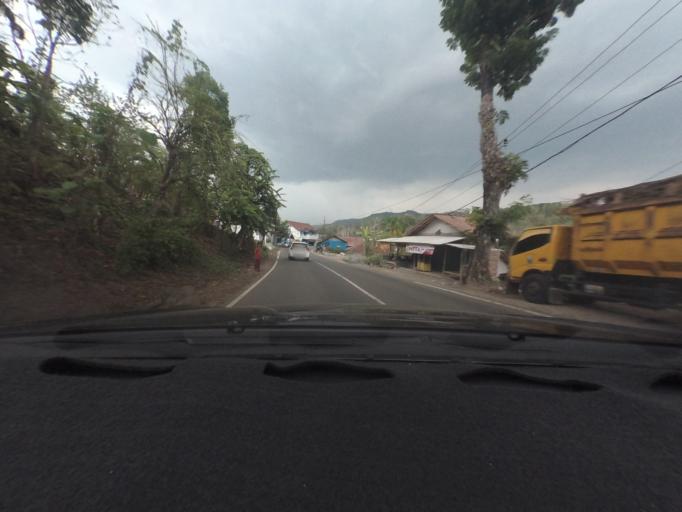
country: ID
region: West Java
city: Sindangsari
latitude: -6.9919
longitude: 106.6712
